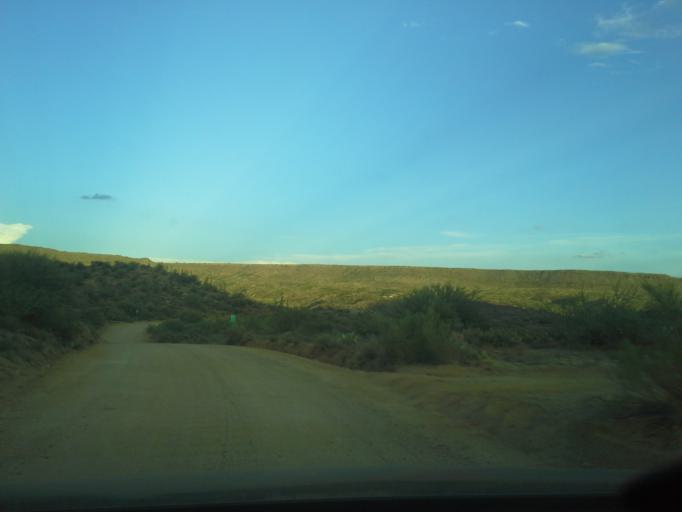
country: US
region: Arizona
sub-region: Yavapai County
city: Cordes Lakes
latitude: 34.2256
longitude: -112.1513
